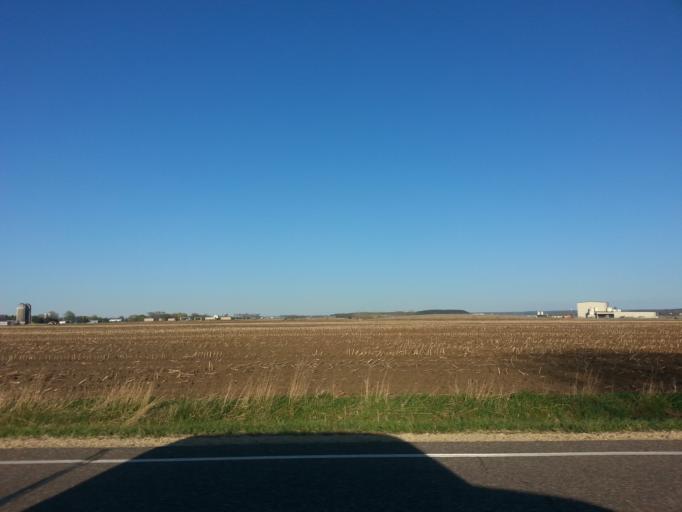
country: US
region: Minnesota
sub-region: Goodhue County
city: Cannon Falls
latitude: 44.5403
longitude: -93.0200
